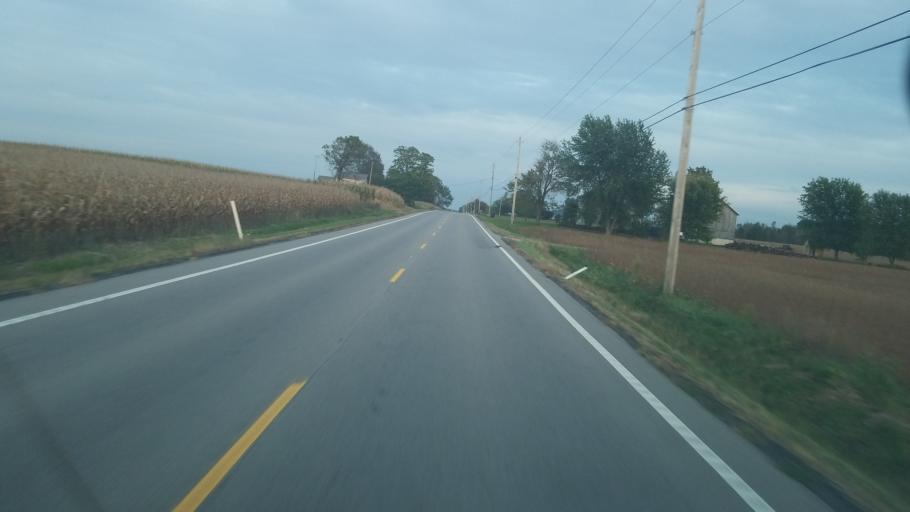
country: US
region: Ohio
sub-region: Ashtabula County
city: Andover
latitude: 41.6069
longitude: -80.6989
